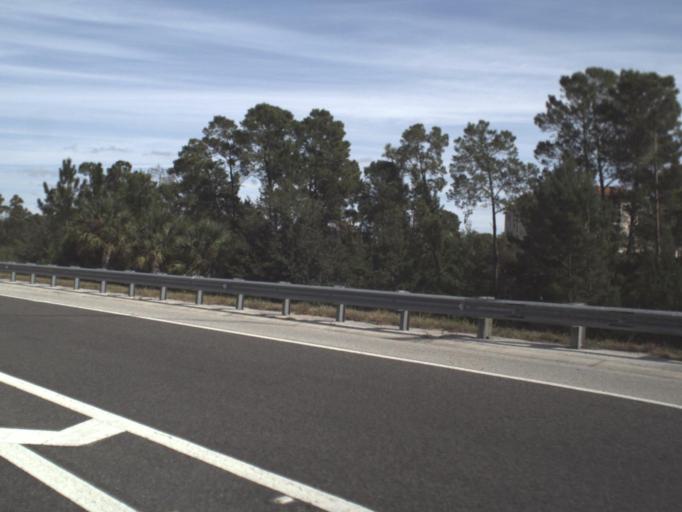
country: US
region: Florida
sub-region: Polk County
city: Citrus Ridge
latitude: 28.3630
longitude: -81.6104
